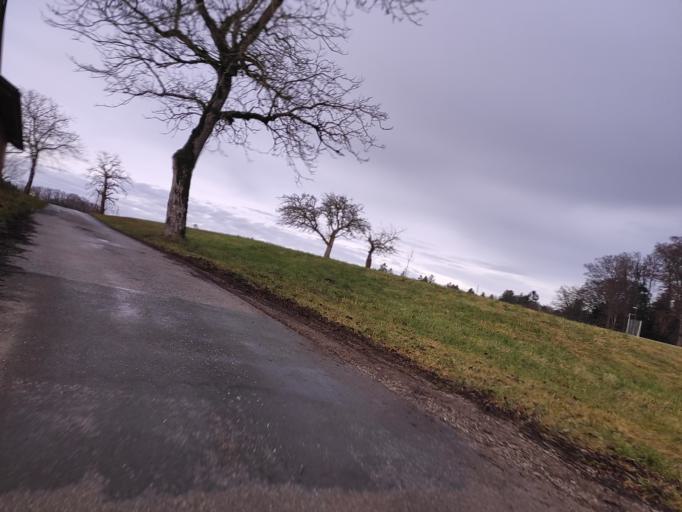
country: AT
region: Salzburg
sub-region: Politischer Bezirk Salzburg-Umgebung
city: Elixhausen
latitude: 47.8758
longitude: 13.0496
